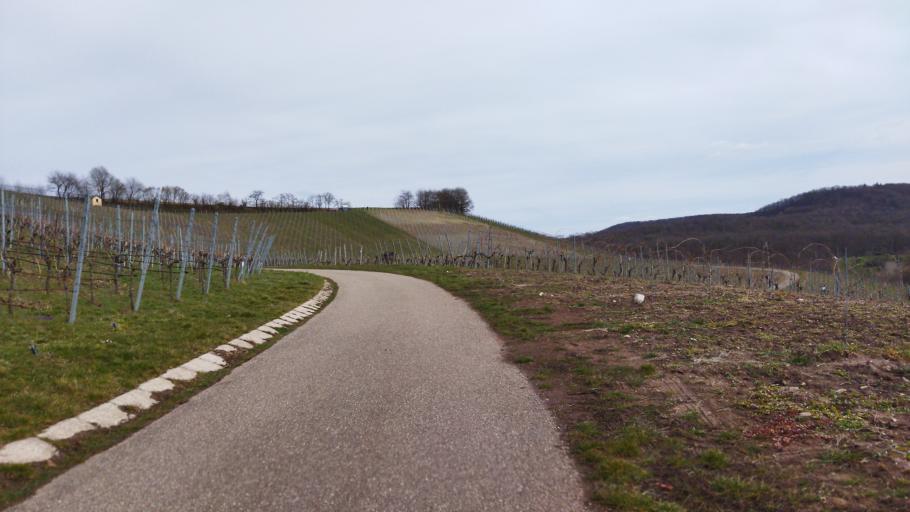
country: DE
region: Baden-Wuerttemberg
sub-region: Regierungsbezirk Stuttgart
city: Bretzfeld
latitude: 49.1762
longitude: 9.4563
